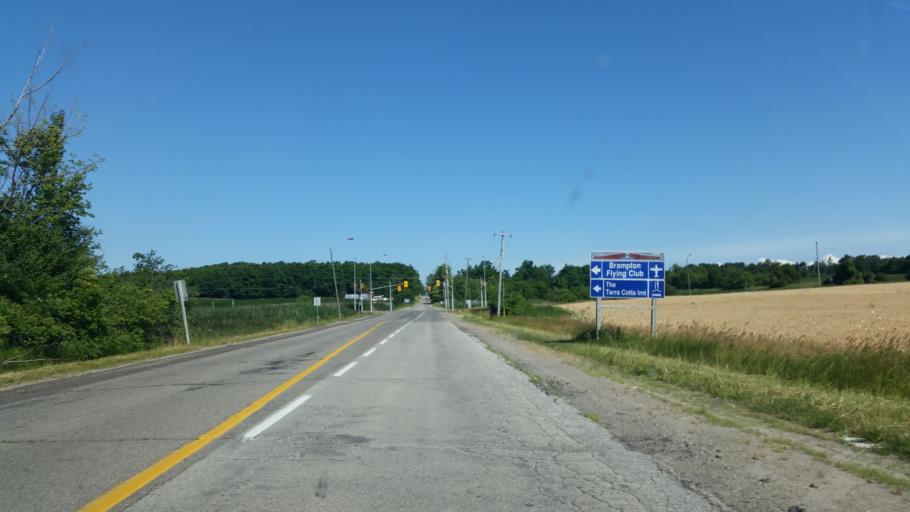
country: CA
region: Ontario
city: Brampton
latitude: 43.7914
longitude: -79.8554
